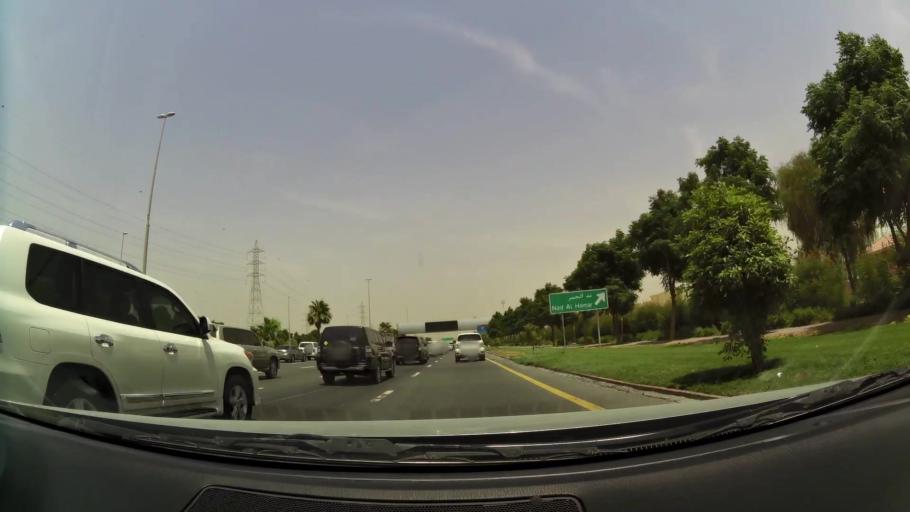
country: AE
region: Ash Shariqah
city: Sharjah
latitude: 25.2125
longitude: 55.3924
